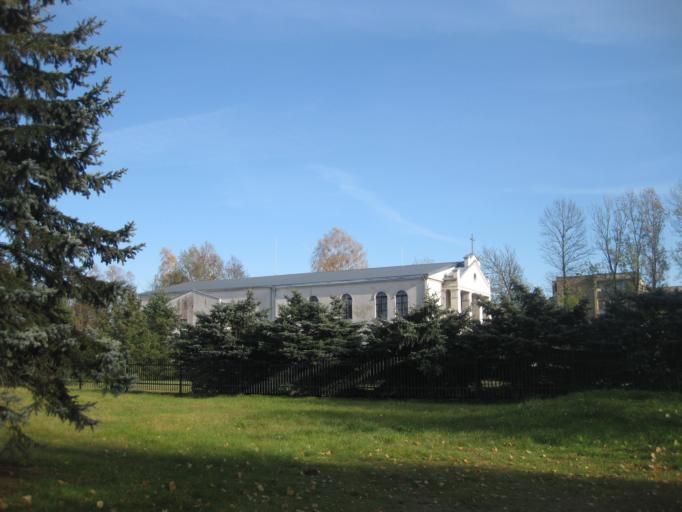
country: LT
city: Ezerelis
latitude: 54.8821
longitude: 23.6028
